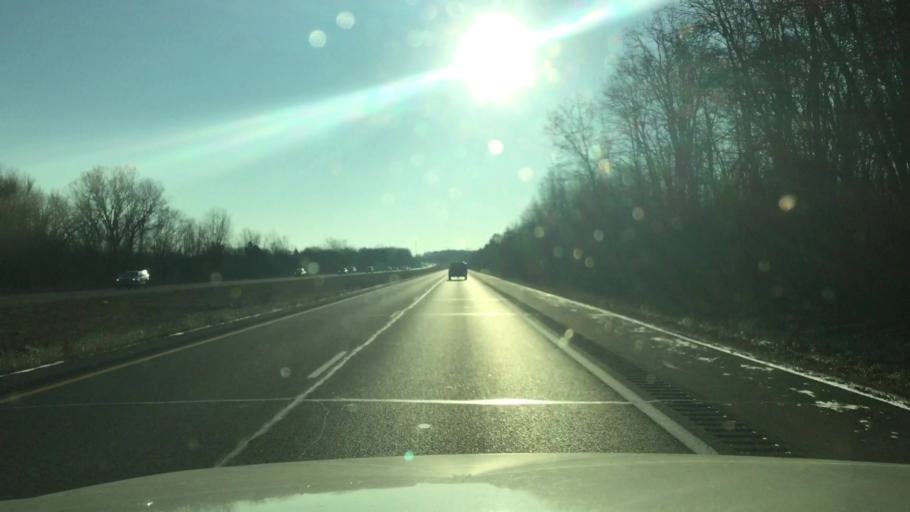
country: US
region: Michigan
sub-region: Genesee County
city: Grand Blanc
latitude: 42.9345
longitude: -83.7003
